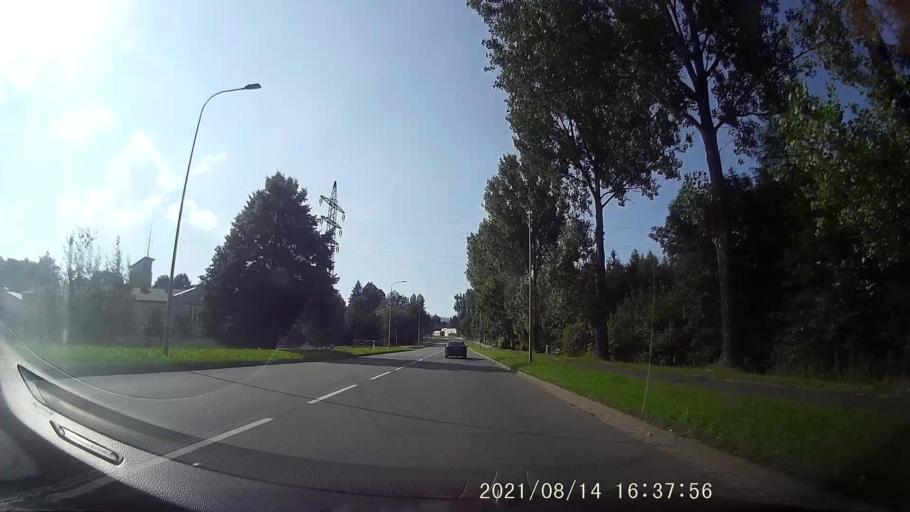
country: PL
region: Lower Silesian Voivodeship
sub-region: Powiat kamiennogorski
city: Kamienna Gora
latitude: 50.7883
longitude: 16.0375
